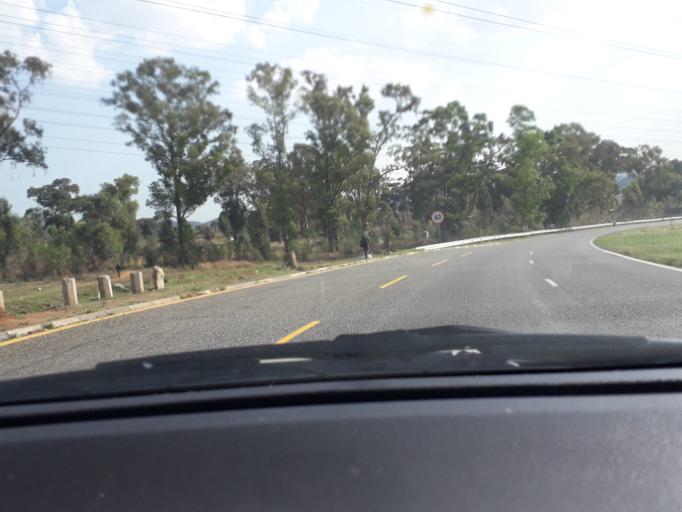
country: ZA
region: Gauteng
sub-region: City of Johannesburg Metropolitan Municipality
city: Modderfontein
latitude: -26.1263
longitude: 28.1330
